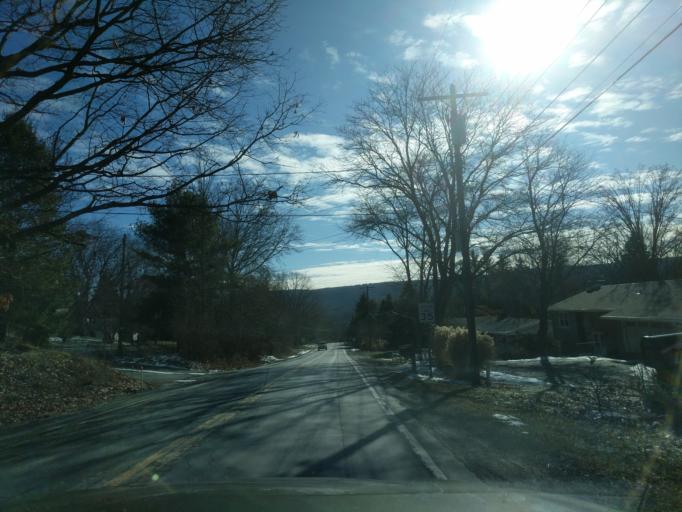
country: US
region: New York
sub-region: Tompkins County
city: East Ithaca
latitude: 42.4260
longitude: -76.4618
